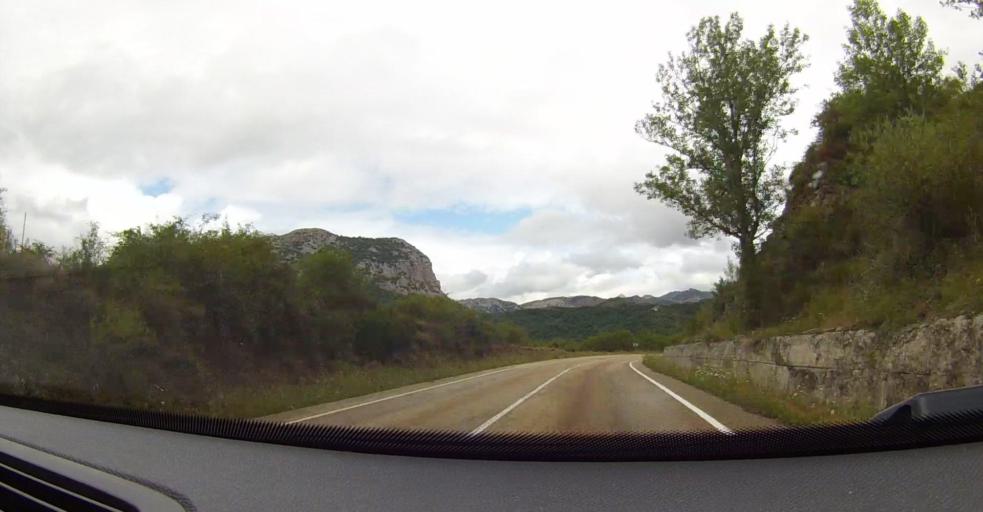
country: ES
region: Castille and Leon
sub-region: Provincia de Leon
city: Reyero
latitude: 42.9412
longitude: -5.2628
